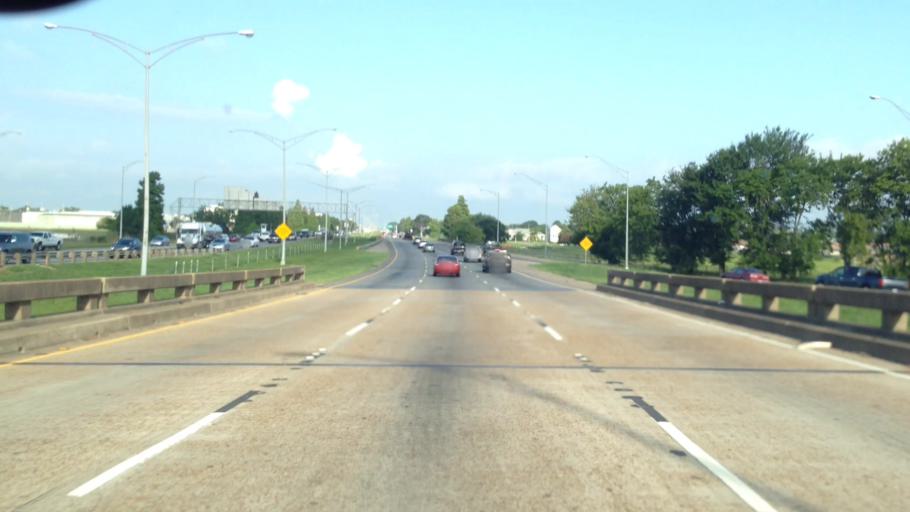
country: US
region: Louisiana
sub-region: Jefferson Parish
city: Kenner
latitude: 30.0096
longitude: -90.2423
